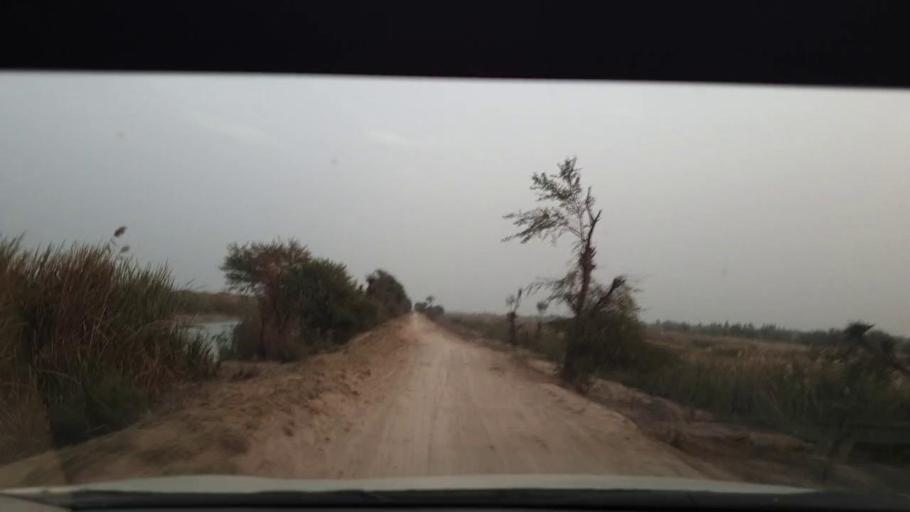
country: PK
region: Sindh
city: Berani
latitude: 25.8615
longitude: 68.7754
